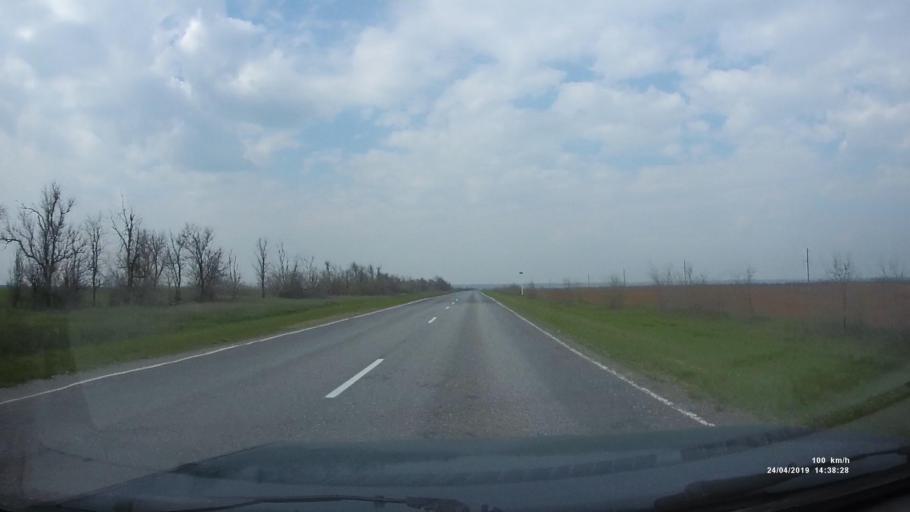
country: RU
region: Rostov
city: Remontnoye
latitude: 46.4017
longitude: 43.8861
